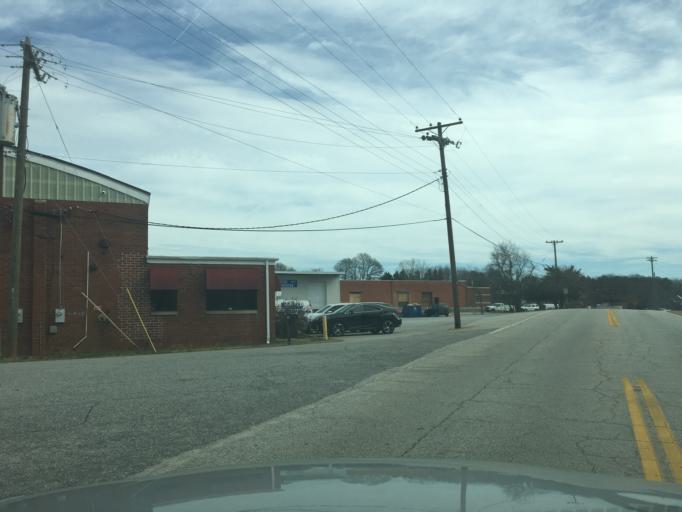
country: US
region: South Carolina
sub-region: Greenville County
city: Greenville
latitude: 34.8449
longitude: -82.3567
